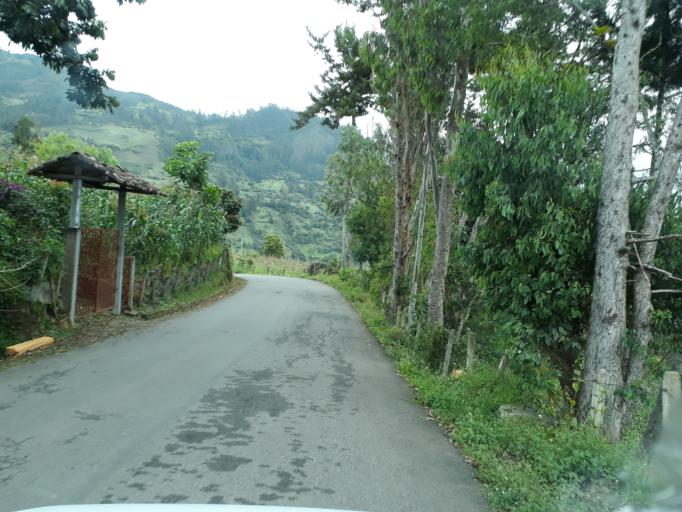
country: CO
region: Cundinamarca
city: Junin
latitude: 4.8168
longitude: -73.6767
